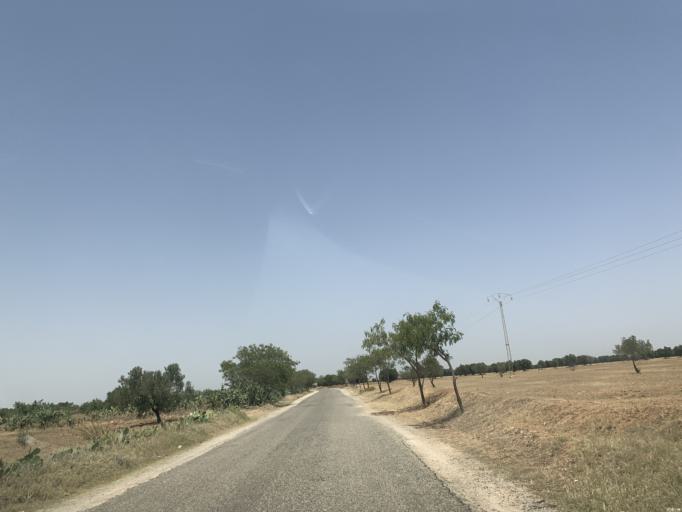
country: TN
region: Al Mahdiyah
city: Shurban
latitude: 35.1820
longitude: 10.2385
